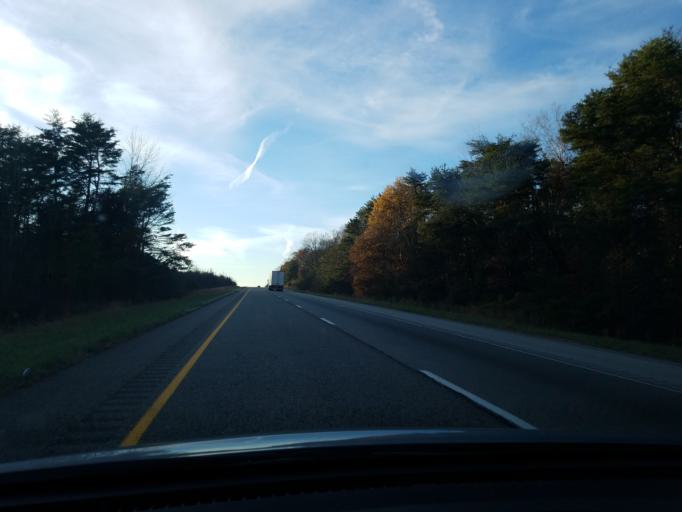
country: US
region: Indiana
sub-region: Warrick County
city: Boonville
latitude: 38.2000
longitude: -87.1847
